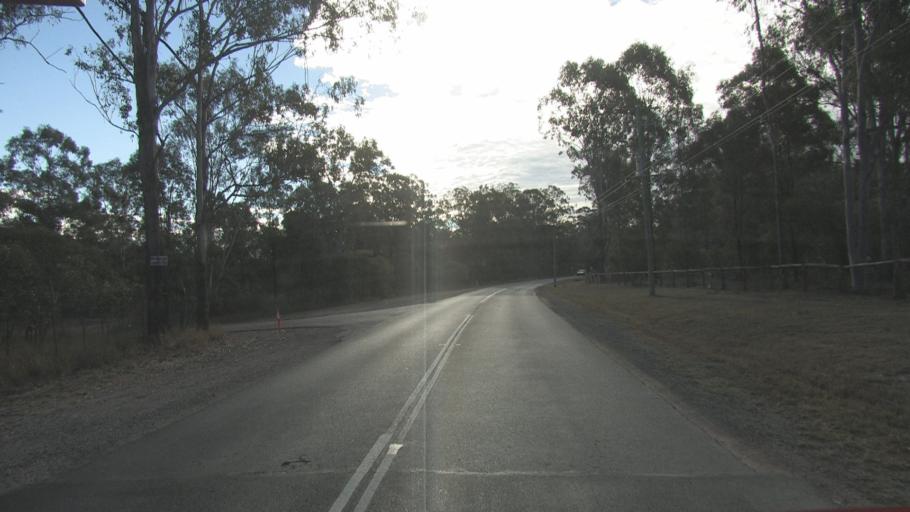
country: AU
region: Queensland
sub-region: Logan
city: Cedar Vale
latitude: -27.8620
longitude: 153.0569
